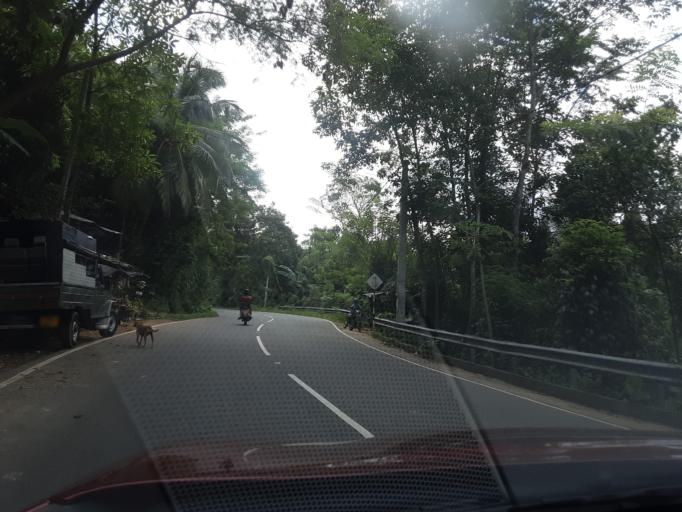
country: LK
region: Uva
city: Monaragala
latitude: 6.8996
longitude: 81.2509
